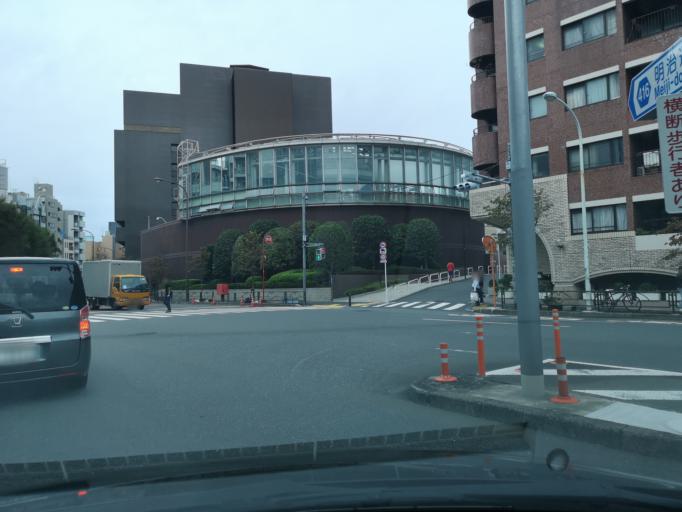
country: JP
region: Tokyo
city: Tokyo
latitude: 35.6466
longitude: 139.7258
